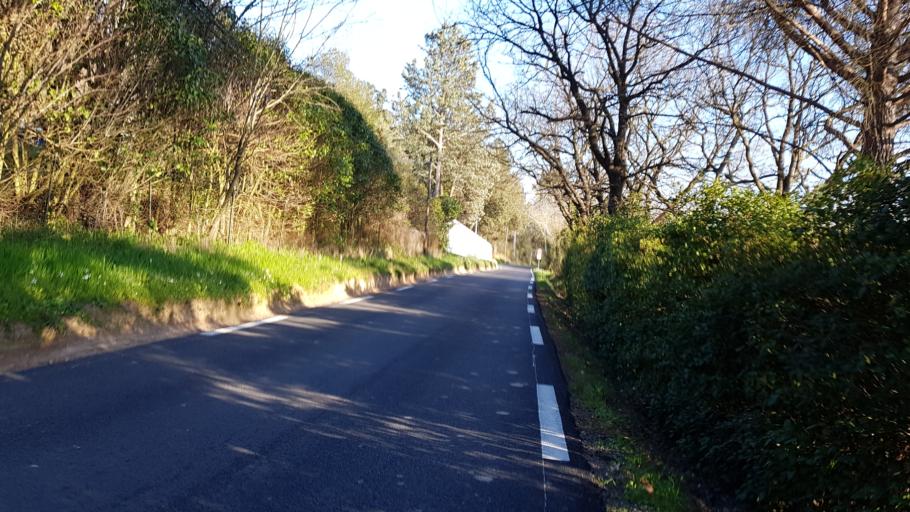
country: FR
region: Provence-Alpes-Cote d'Azur
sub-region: Departement des Bouches-du-Rhone
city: Bouc-Bel-Air
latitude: 43.4971
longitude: 5.4084
